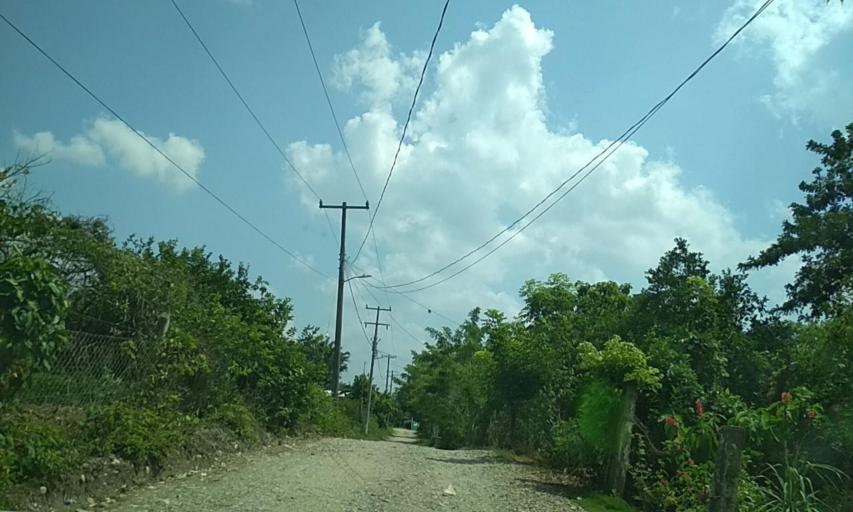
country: MX
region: Puebla
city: San Jose Acateno
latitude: 20.1742
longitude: -97.1087
